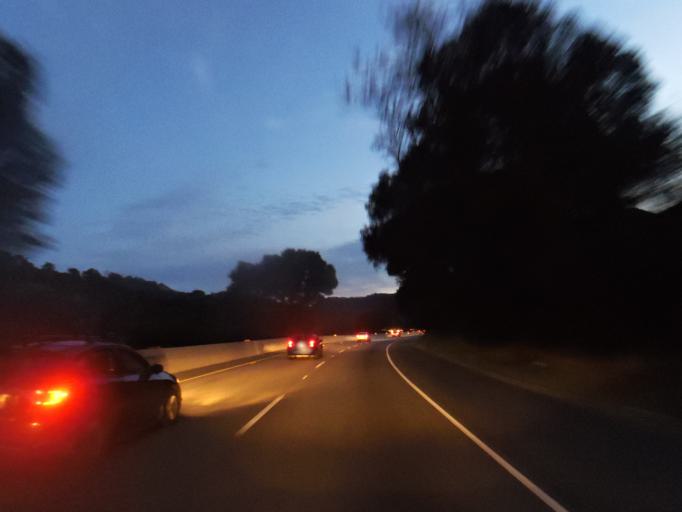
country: US
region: California
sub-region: San Luis Obispo County
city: Santa Margarita
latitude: 35.3645
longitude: -120.6388
